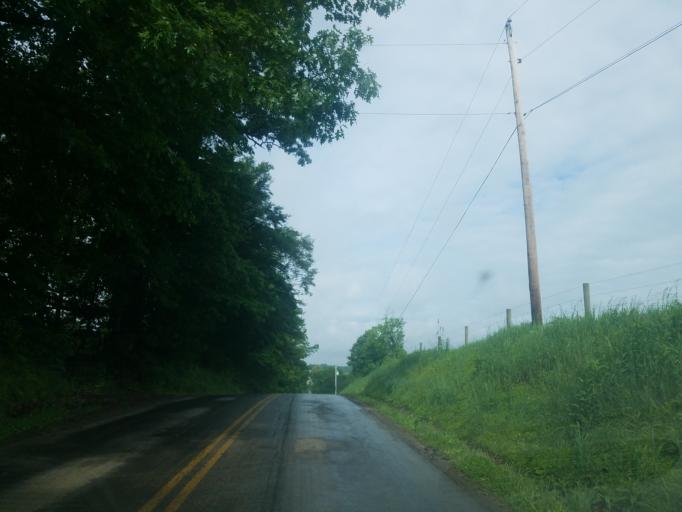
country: US
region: Ohio
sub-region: Holmes County
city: Millersburg
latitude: 40.5079
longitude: -81.8651
